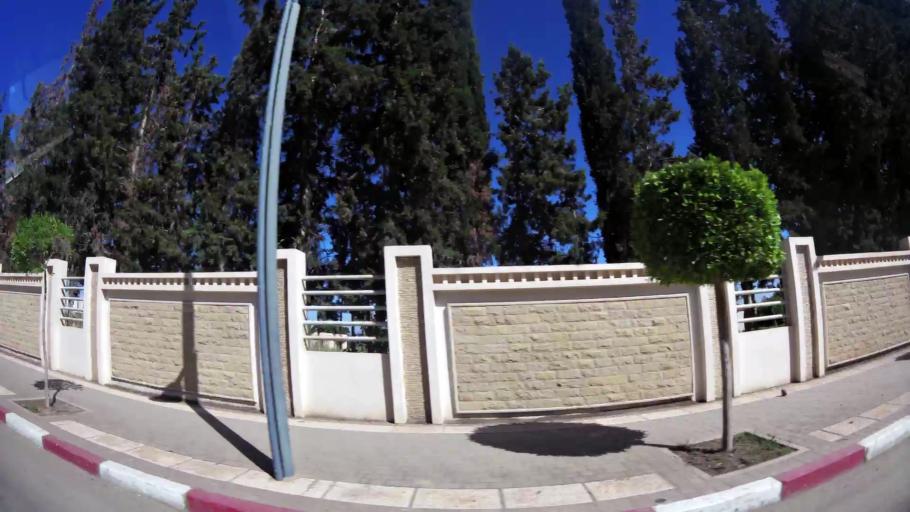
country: MA
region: Oriental
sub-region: Oujda-Angad
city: Oujda
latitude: 34.7188
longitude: -1.9192
